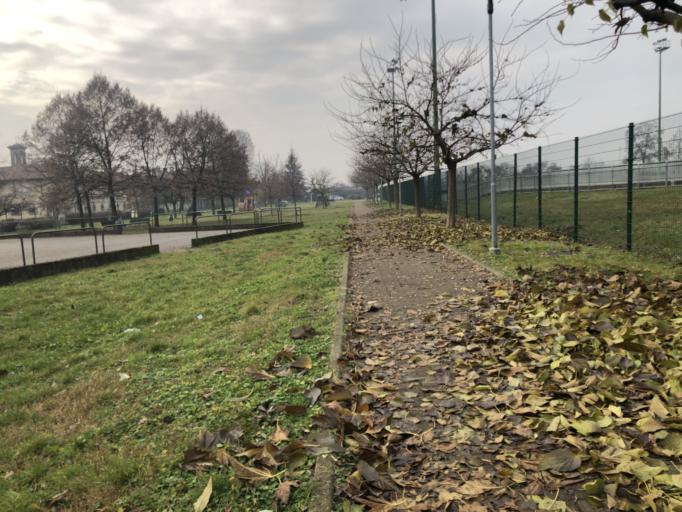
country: IT
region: Lombardy
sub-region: Citta metropolitana di Milano
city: Pregnana Milanese
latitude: 45.5327
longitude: 9.0205
